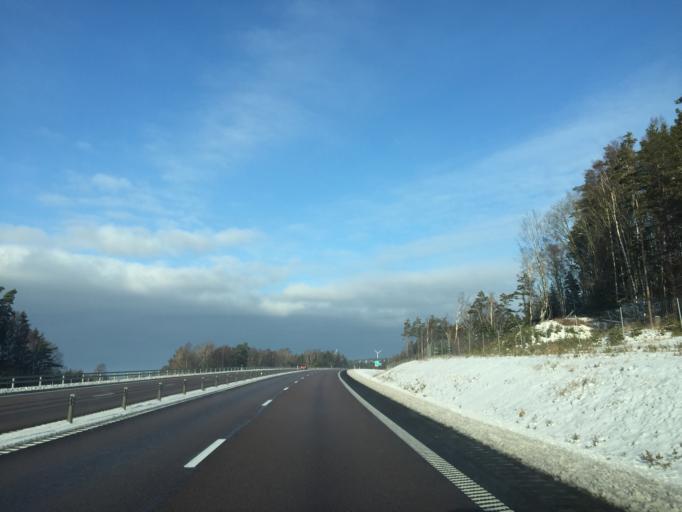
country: SE
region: Vaestra Goetaland
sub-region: Tanums Kommun
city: Tanumshede
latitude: 58.7531
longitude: 11.2855
